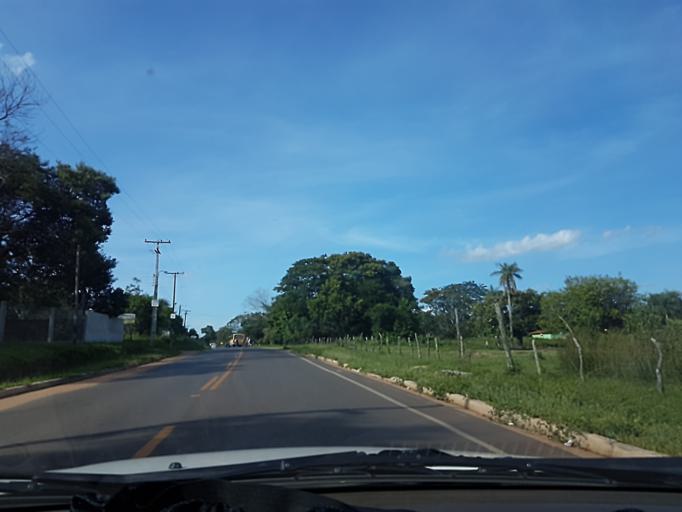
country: PY
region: Central
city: Limpio
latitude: -25.2214
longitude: -57.4479
